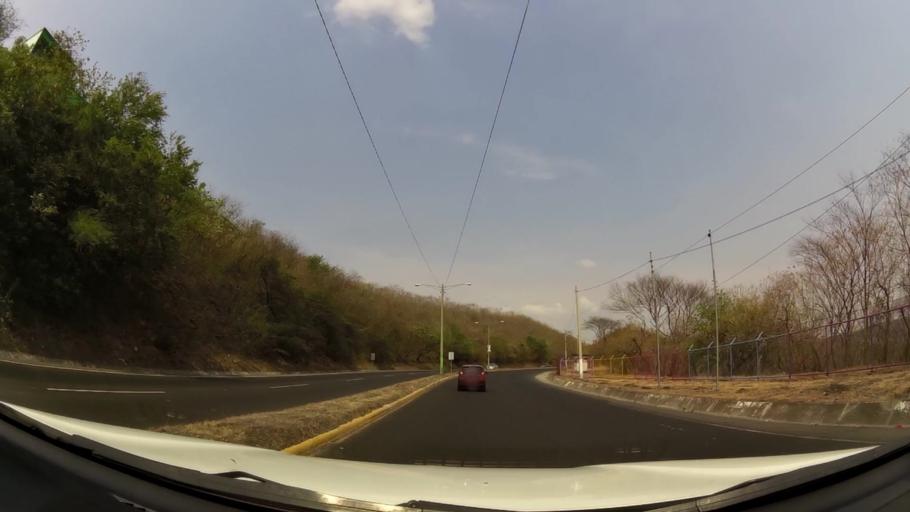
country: NI
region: Managua
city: Ciudad Sandino
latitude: 12.1320
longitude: -86.3166
